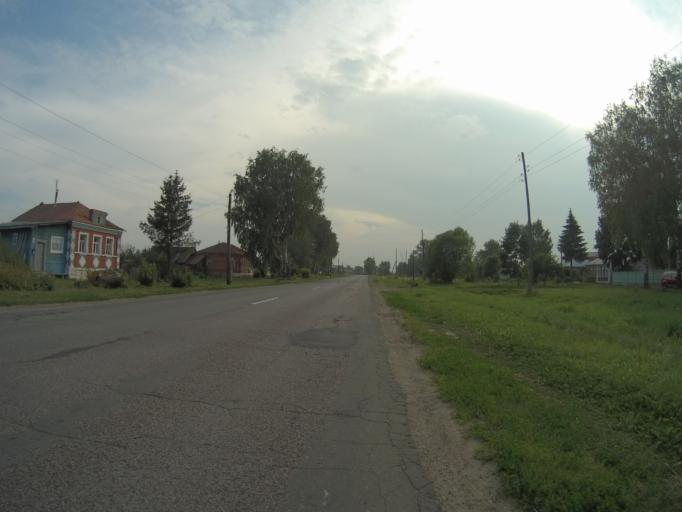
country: RU
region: Vladimir
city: Suzdal'
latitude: 56.4068
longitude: 40.3471
